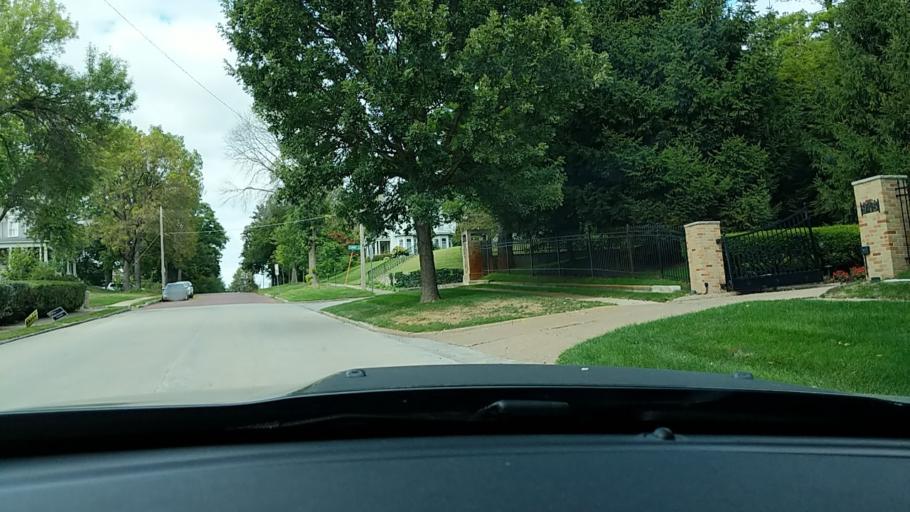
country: US
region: Iowa
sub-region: Scott County
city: Davenport
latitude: 41.5302
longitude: -90.5538
